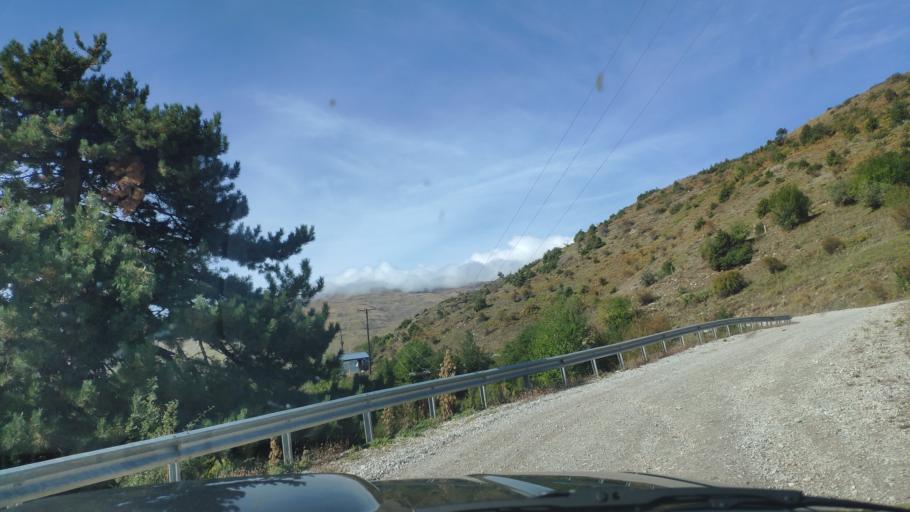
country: AL
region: Korce
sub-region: Rrethi i Devollit
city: Miras
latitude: 40.4012
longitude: 20.8502
